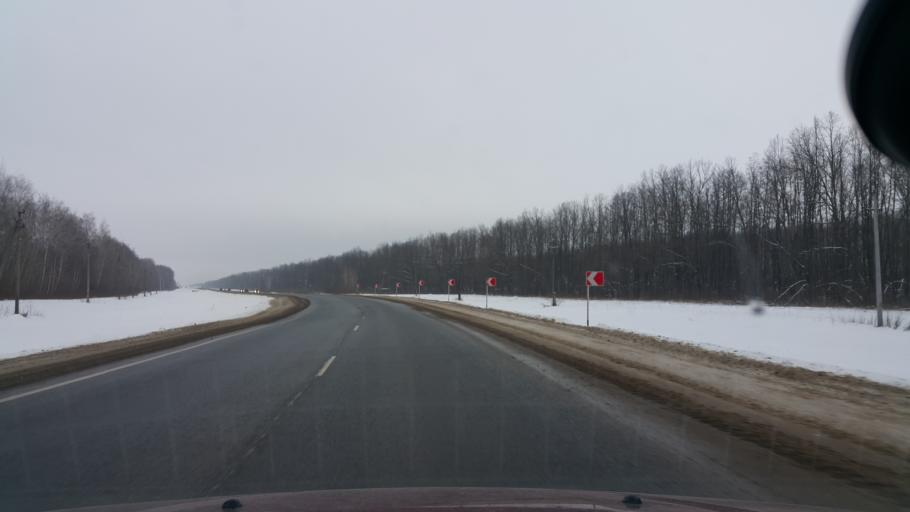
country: RU
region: Tambov
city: Bokino
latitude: 52.5990
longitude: 41.4433
